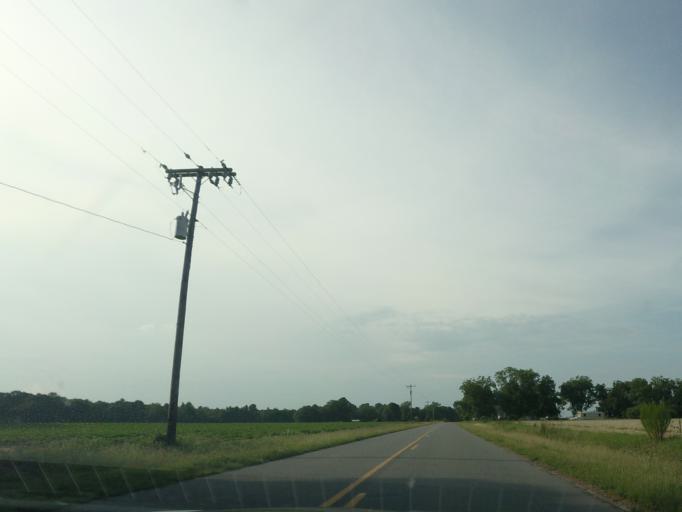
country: US
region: Georgia
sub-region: Bleckley County
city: Cochran
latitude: 32.5170
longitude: -83.3057
